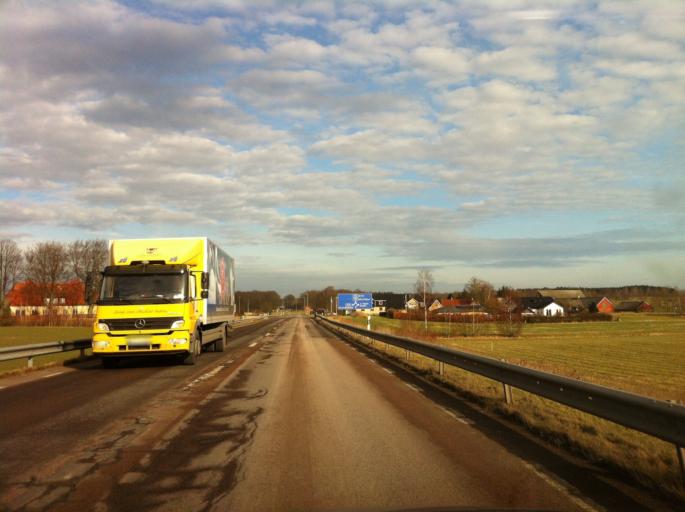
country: SE
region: Skane
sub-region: Bjuvs Kommun
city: Billesholm
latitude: 56.0031
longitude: 12.9516
